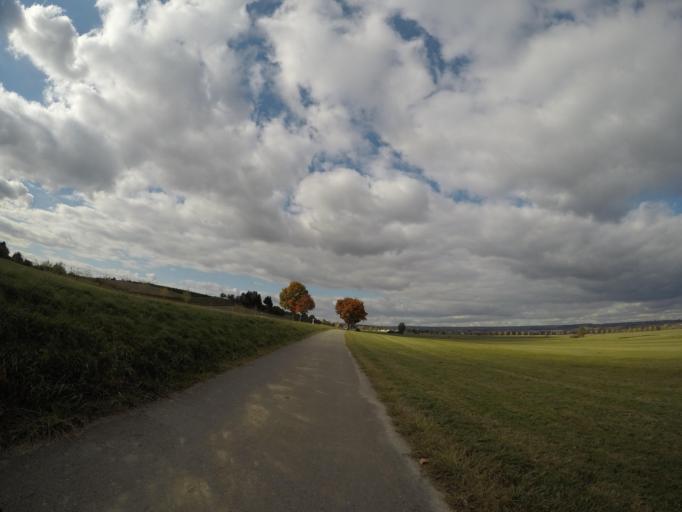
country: DE
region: Baden-Wuerttemberg
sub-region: Tuebingen Region
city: Unterstadion
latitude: 48.2087
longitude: 9.6732
